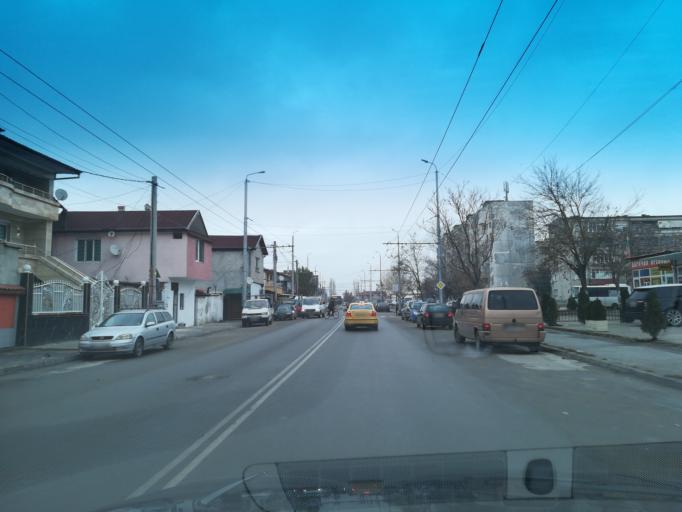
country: BG
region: Plovdiv
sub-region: Obshtina Plovdiv
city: Plovdiv
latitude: 42.1567
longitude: 24.7883
